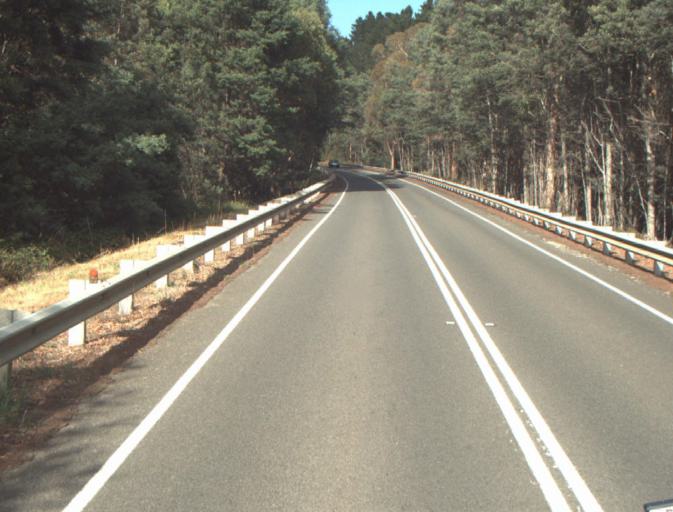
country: AU
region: Tasmania
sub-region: Launceston
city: Mayfield
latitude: -41.2990
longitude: 147.2091
